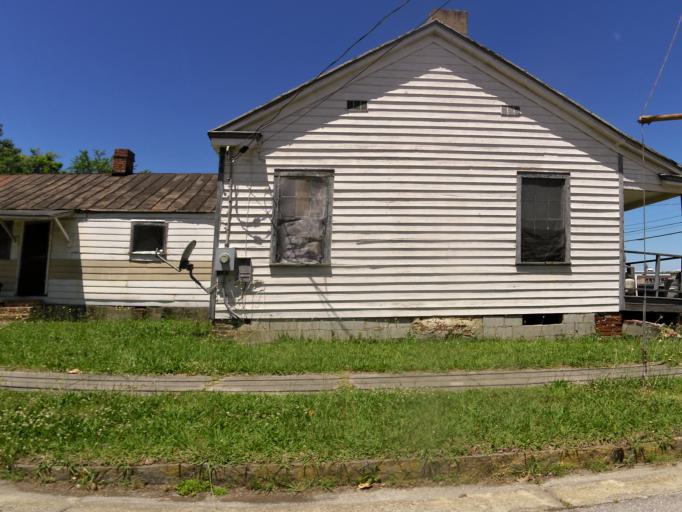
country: US
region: Georgia
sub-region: Richmond County
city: Augusta
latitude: 33.4685
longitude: -81.9754
